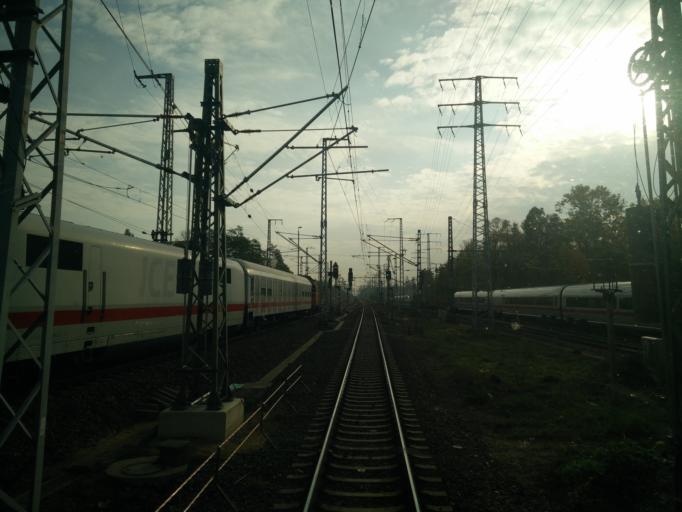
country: DE
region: Berlin
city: Karlshorst
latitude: 52.4853
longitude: 13.5159
